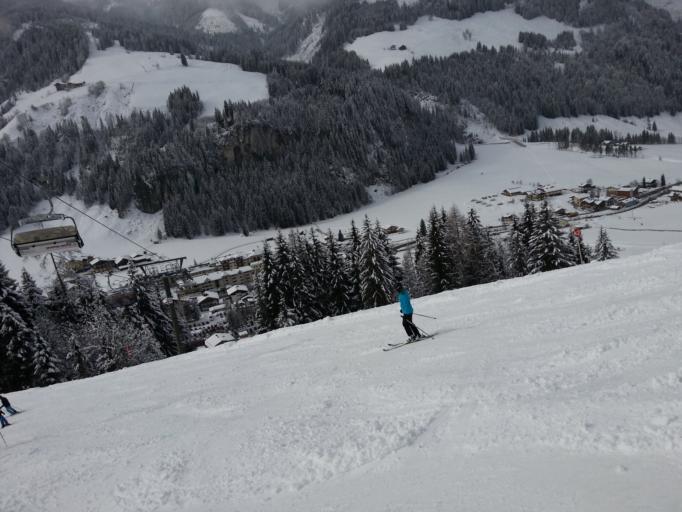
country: AT
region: Salzburg
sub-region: Politischer Bezirk Sankt Johann im Pongau
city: Kleinarl
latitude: 47.2826
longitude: 13.3231
